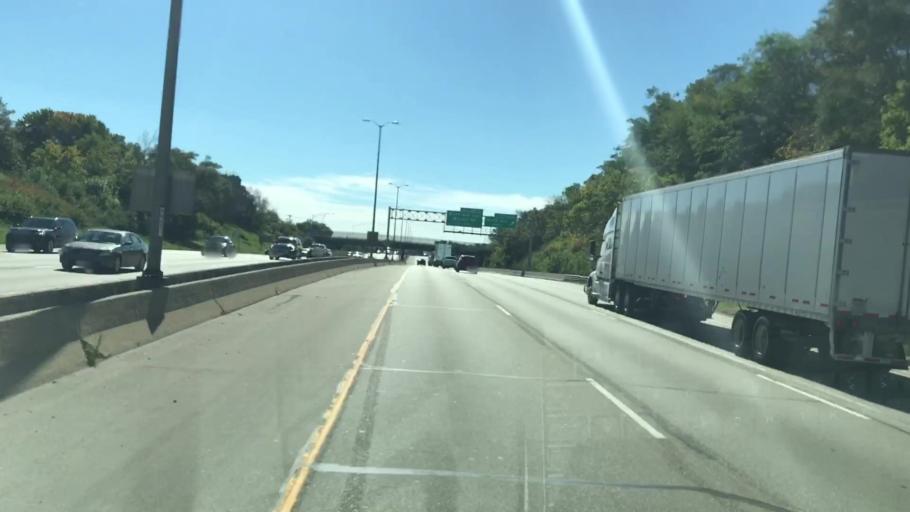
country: US
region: Wisconsin
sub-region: Waukesha County
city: Elm Grove
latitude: 43.0650
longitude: -88.0534
